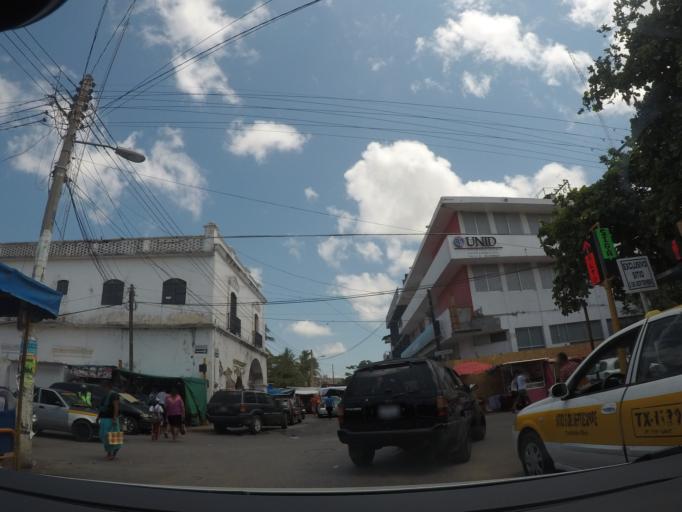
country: MX
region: Oaxaca
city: Juchitan de Zaragoza
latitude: 16.4339
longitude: -95.0226
